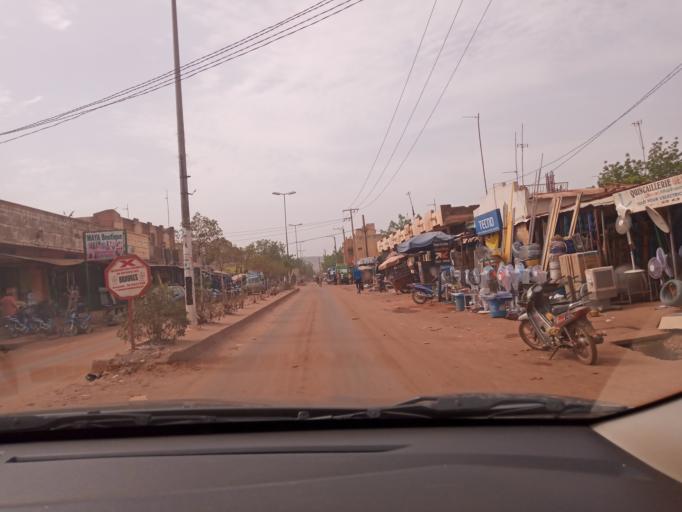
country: ML
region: Bamako
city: Bamako
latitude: 12.6748
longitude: -7.9242
